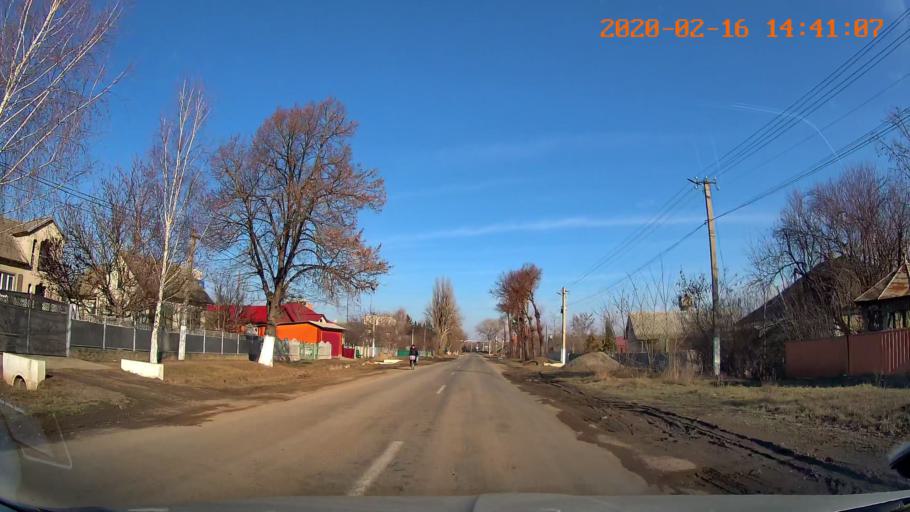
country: RO
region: Botosani
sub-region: Comuna Darabani
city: Bajura
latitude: 48.2520
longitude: 26.5672
